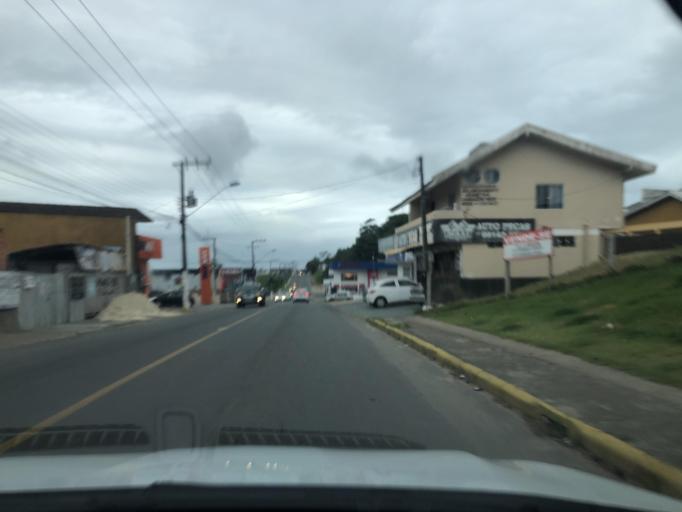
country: BR
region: Santa Catarina
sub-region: Barra Velha
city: Barra Velha
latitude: -26.6381
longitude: -48.6923
